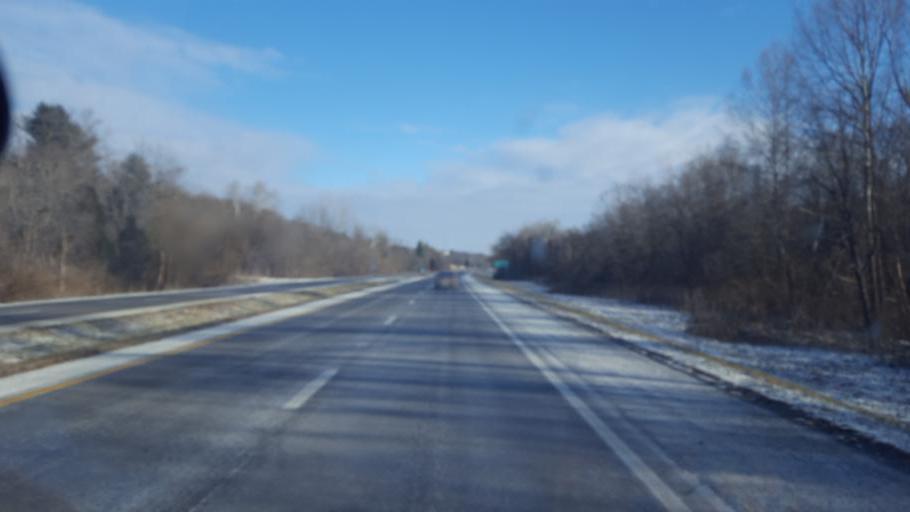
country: US
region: Ohio
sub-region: Ross County
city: Chillicothe
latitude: 39.2697
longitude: -82.9651
